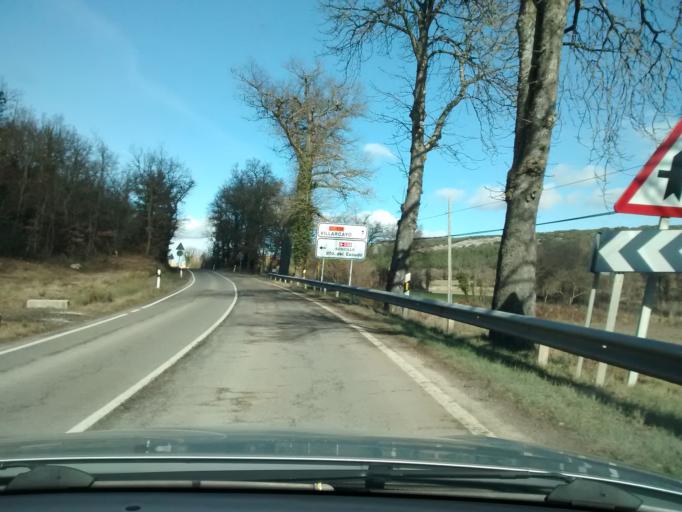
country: ES
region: Castille and Leon
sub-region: Provincia de Burgos
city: Medina de Pomar
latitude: 42.8979
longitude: -3.5886
